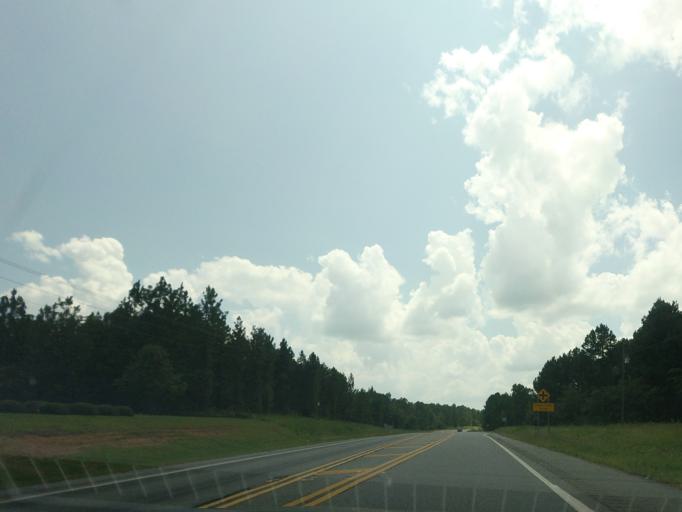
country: US
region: Georgia
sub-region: Bleckley County
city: Cochran
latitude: 32.3855
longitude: -83.3269
